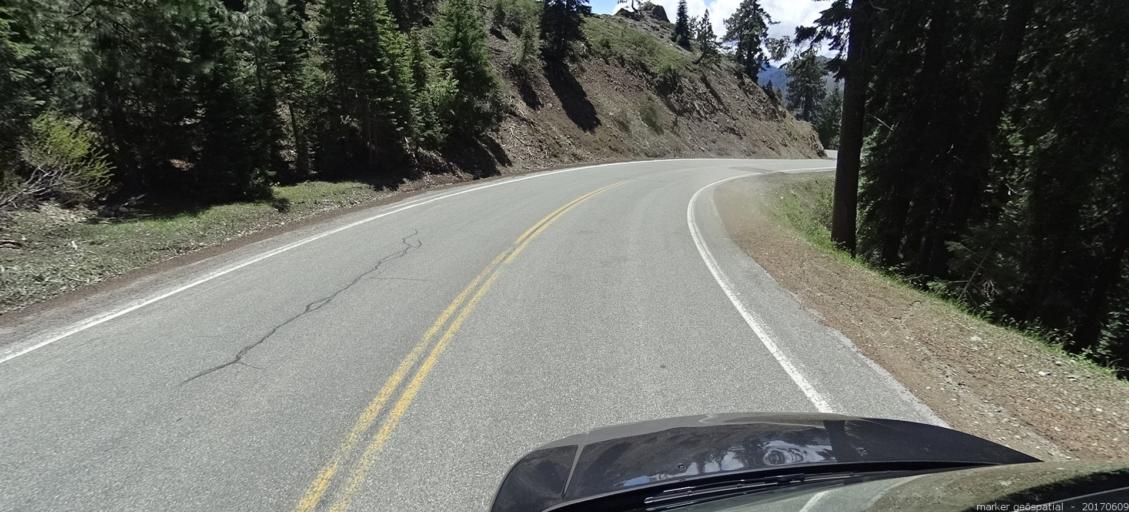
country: US
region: California
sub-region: Siskiyou County
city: Yreka
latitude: 41.3902
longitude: -122.9922
